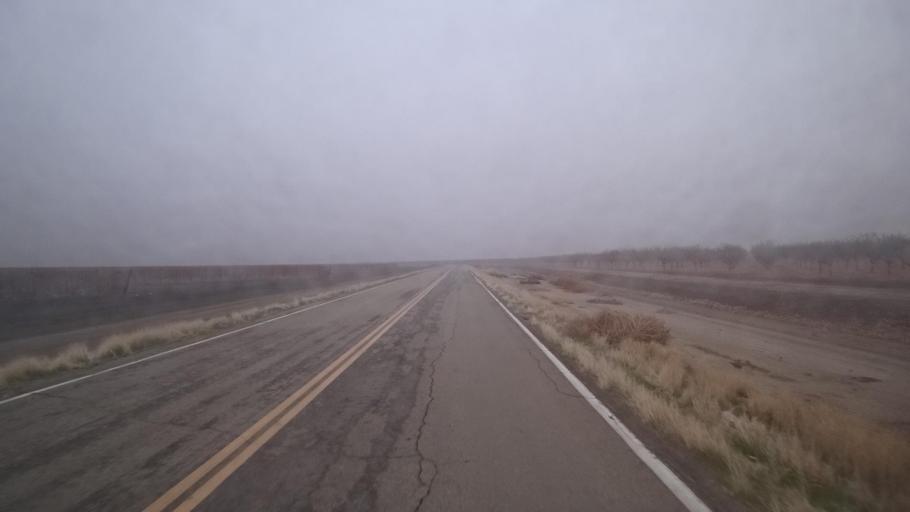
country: US
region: California
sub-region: Kern County
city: Buttonwillow
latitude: 35.4240
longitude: -119.5304
